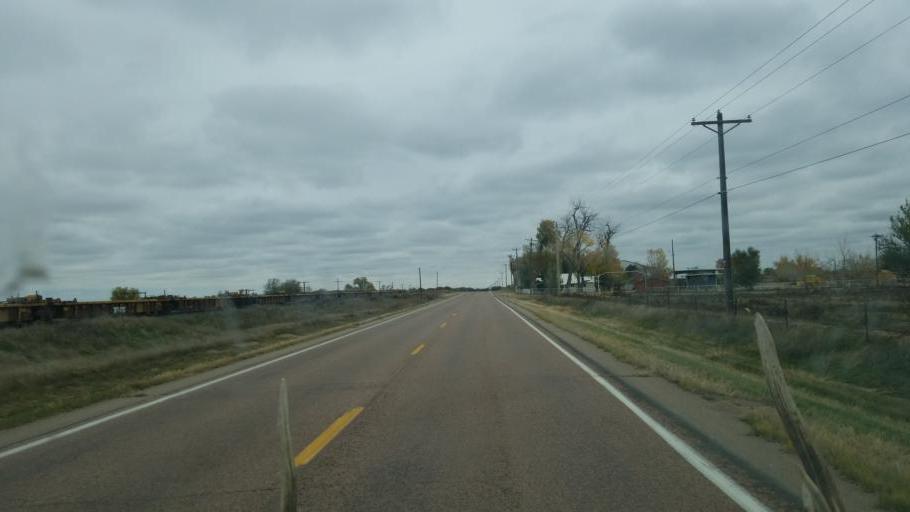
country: US
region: Colorado
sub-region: Crowley County
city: Ordway
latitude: 38.1860
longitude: -103.8773
